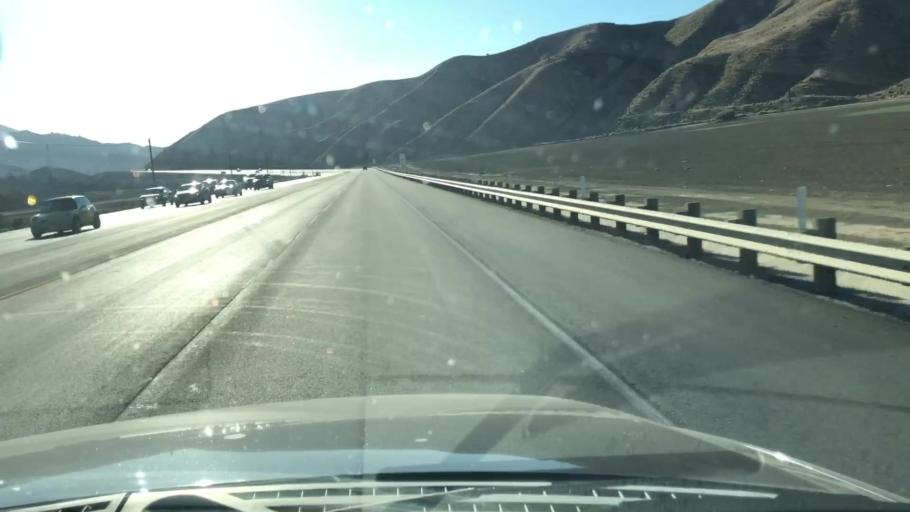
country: US
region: California
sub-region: Los Angeles County
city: Val Verde
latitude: 34.4059
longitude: -118.6960
